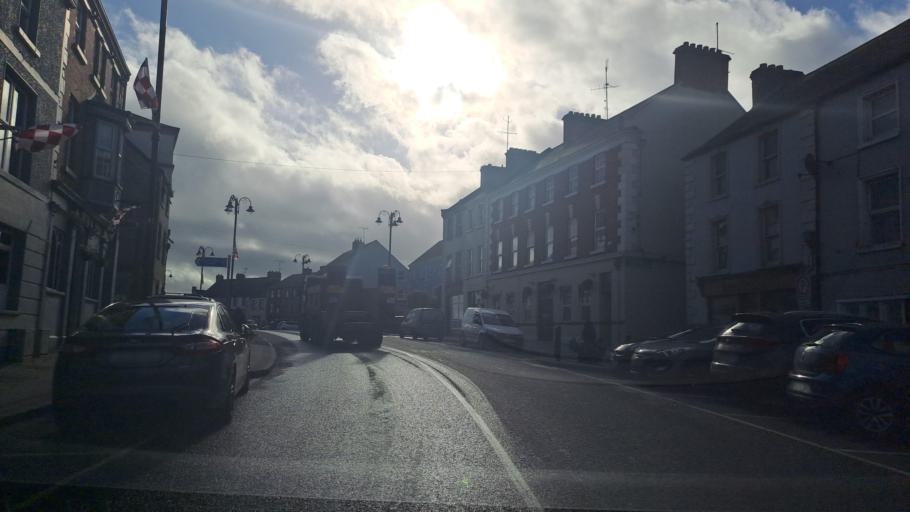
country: IE
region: Ulster
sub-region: County Monaghan
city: Monaghan
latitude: 54.1284
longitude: -6.9030
